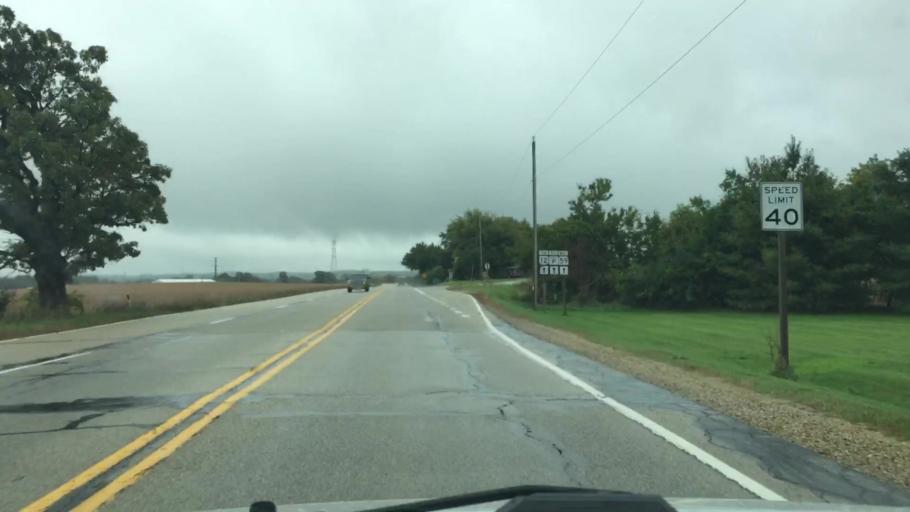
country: US
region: Wisconsin
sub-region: Walworth County
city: Whitewater
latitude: 42.8257
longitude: -88.7047
